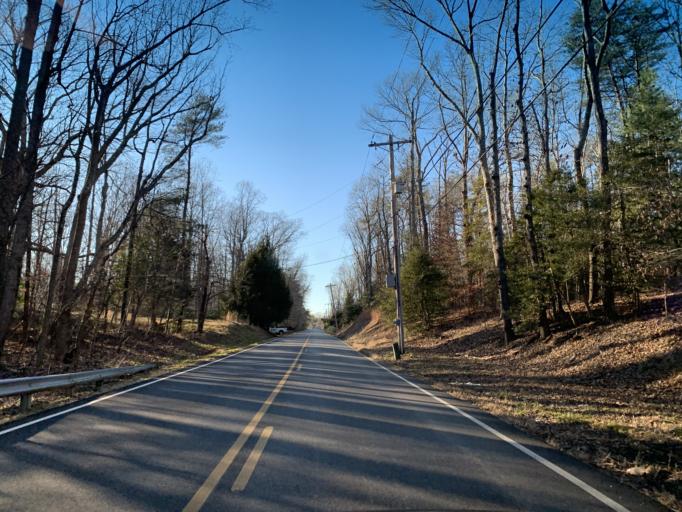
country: US
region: Maryland
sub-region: Saint Mary's County
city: Golden Beach
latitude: 38.4595
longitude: -76.6879
